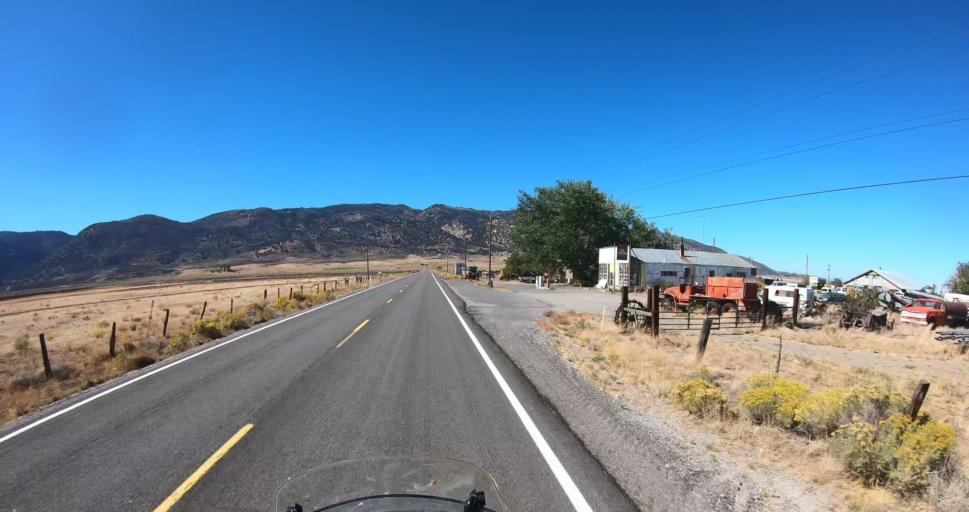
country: US
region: Oregon
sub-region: Lake County
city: Lakeview
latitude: 42.6155
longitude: -120.4920
